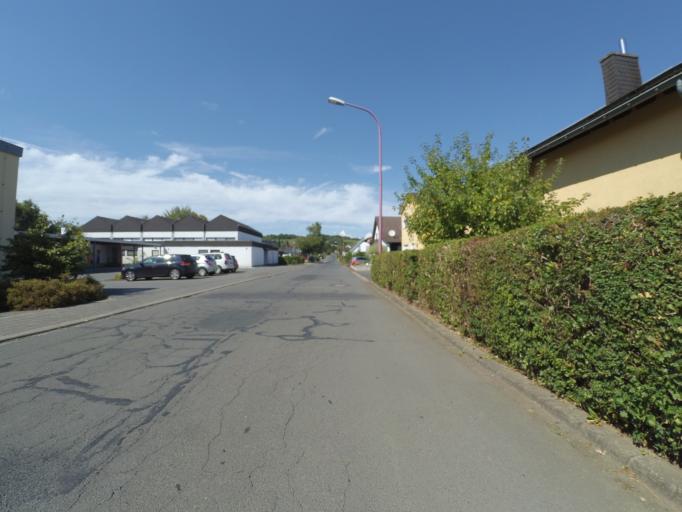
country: DE
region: Rheinland-Pfalz
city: Mehren
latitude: 50.1781
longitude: 6.8753
